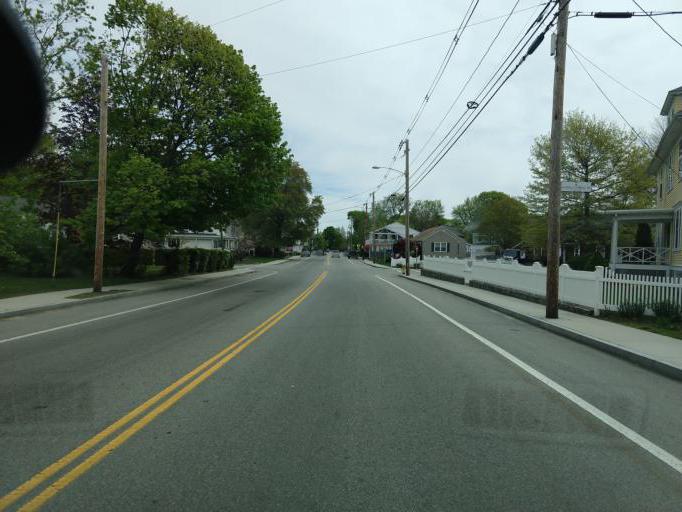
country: US
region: Massachusetts
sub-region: Essex County
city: Haverhill
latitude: 42.7640
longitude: -71.0846
